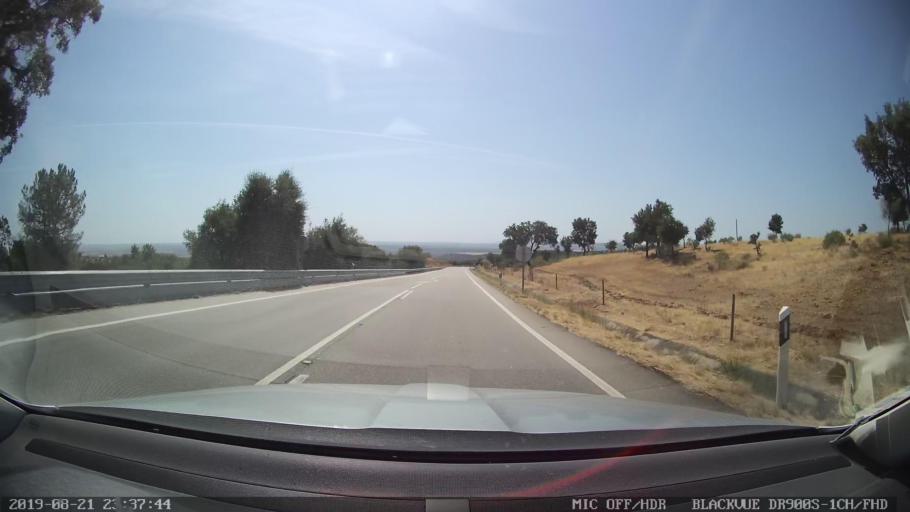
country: PT
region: Guarda
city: Alcains
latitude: 39.8663
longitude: -7.3567
